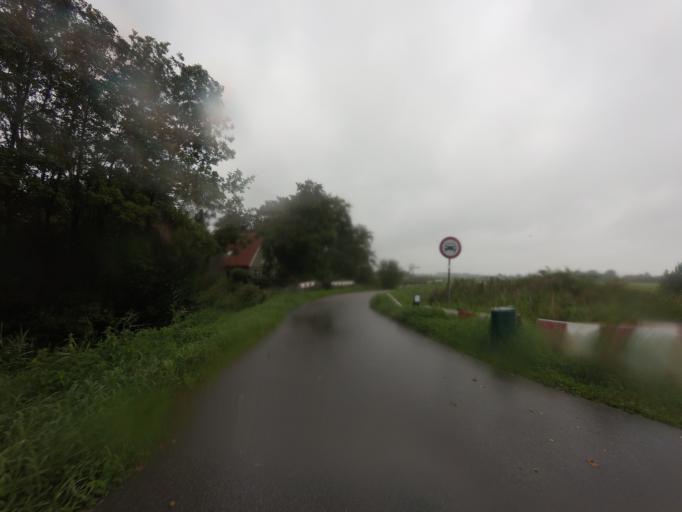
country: NL
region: Friesland
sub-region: Gemeente Smallingerland
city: Oudega
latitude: 53.1024
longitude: 5.9765
